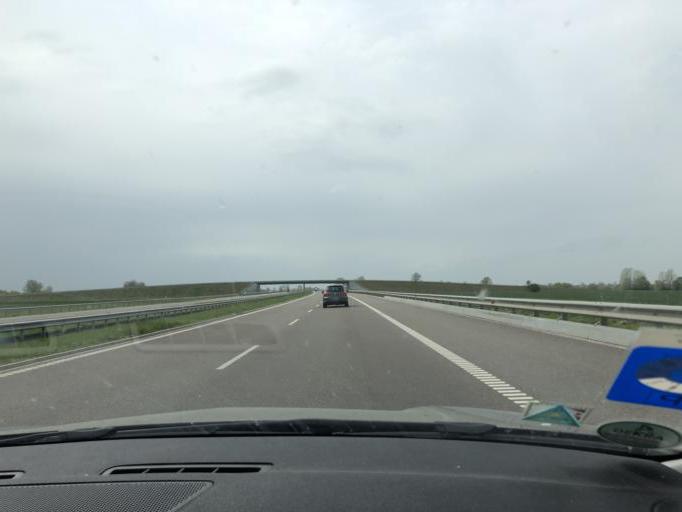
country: PL
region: Subcarpathian Voivodeship
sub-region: Powiat jaroslawski
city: Sosnica
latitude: 49.9262
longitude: 22.8962
